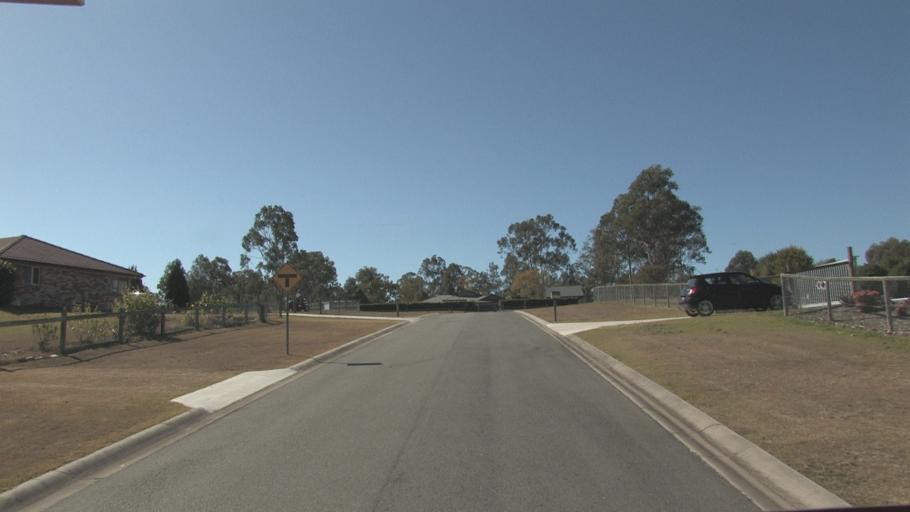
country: AU
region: Queensland
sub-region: Logan
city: Cedar Vale
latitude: -27.8597
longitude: 153.0450
